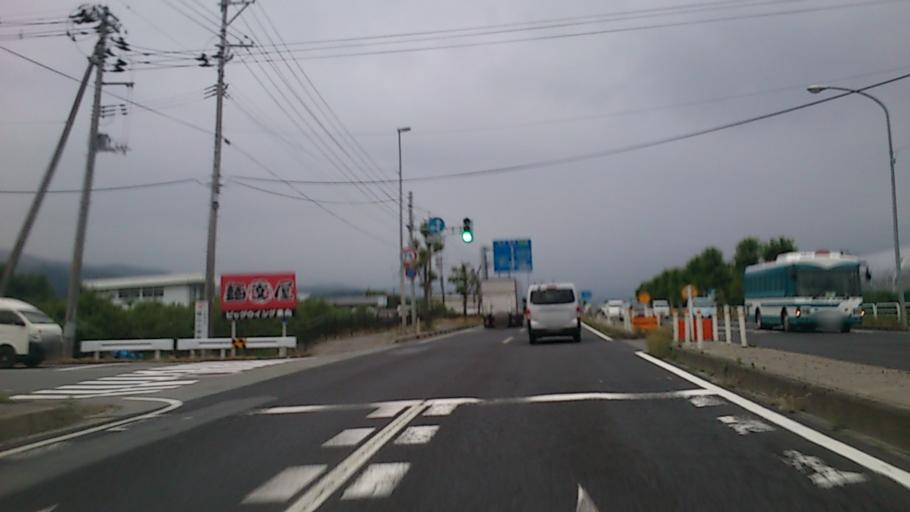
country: JP
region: Yamagata
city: Tendo
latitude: 38.3057
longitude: 140.3633
